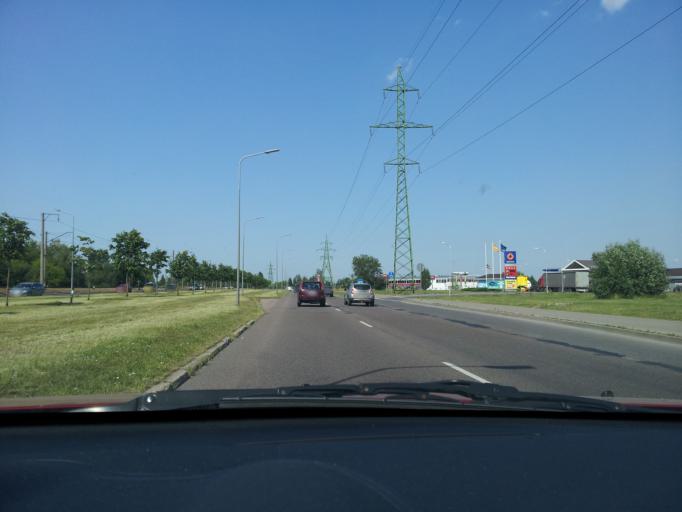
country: LV
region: Riga
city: Jaunciems
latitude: 57.0231
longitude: 24.1358
